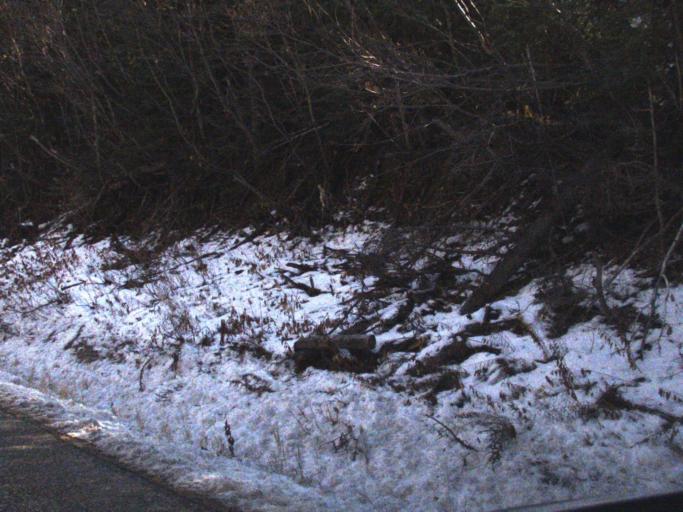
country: US
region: Washington
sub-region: Ferry County
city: Republic
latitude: 48.6053
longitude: -118.4896
